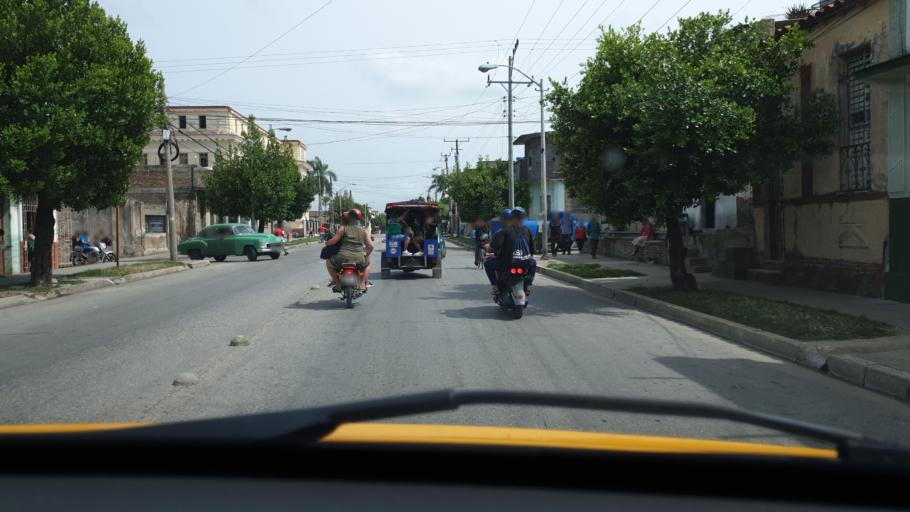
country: CU
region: Villa Clara
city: Santa Clara
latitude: 22.3983
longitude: -79.9633
